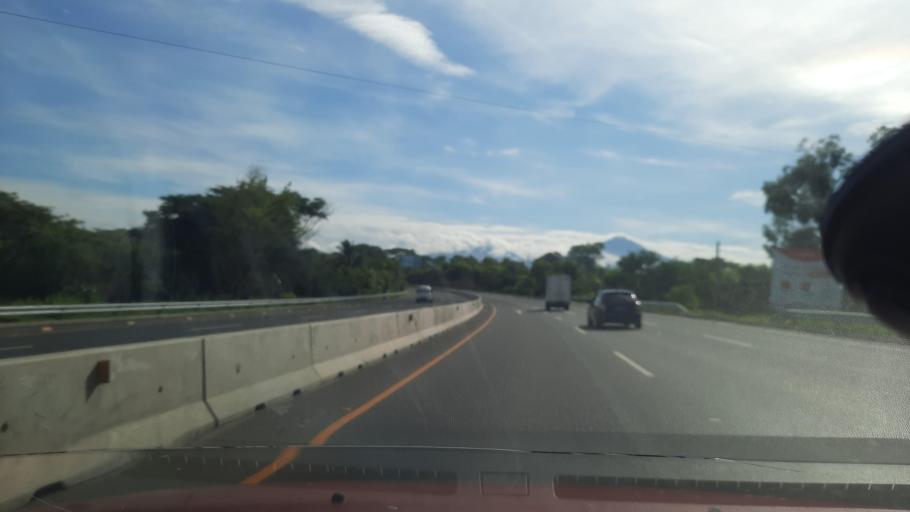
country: SV
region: La Paz
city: El Rosario
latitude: 13.4658
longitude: -89.0063
